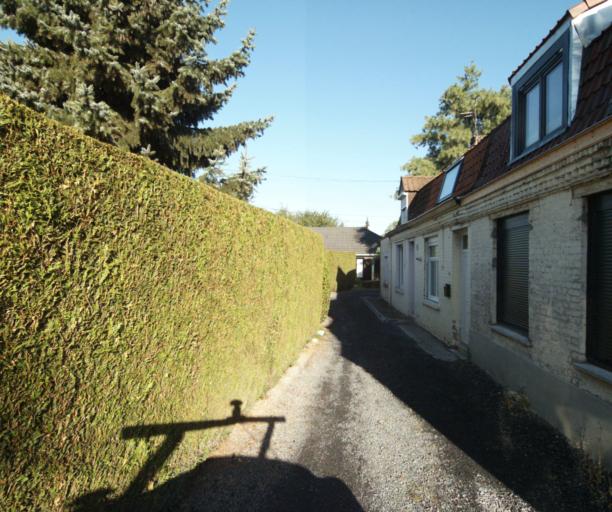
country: FR
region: Nord-Pas-de-Calais
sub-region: Departement du Nord
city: Lys-lez-Lannoy
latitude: 50.6657
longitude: 3.2253
